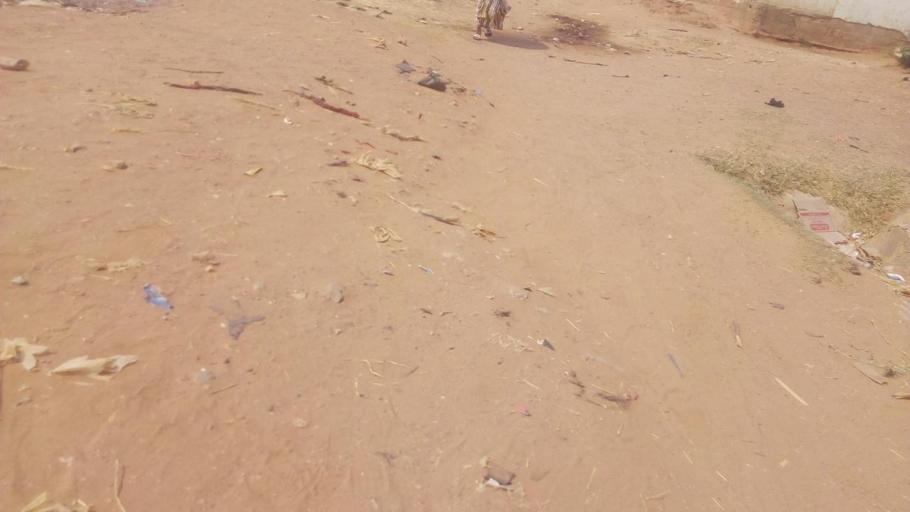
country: ZM
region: Lusaka
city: Lusaka
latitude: -15.3576
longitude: 28.2960
